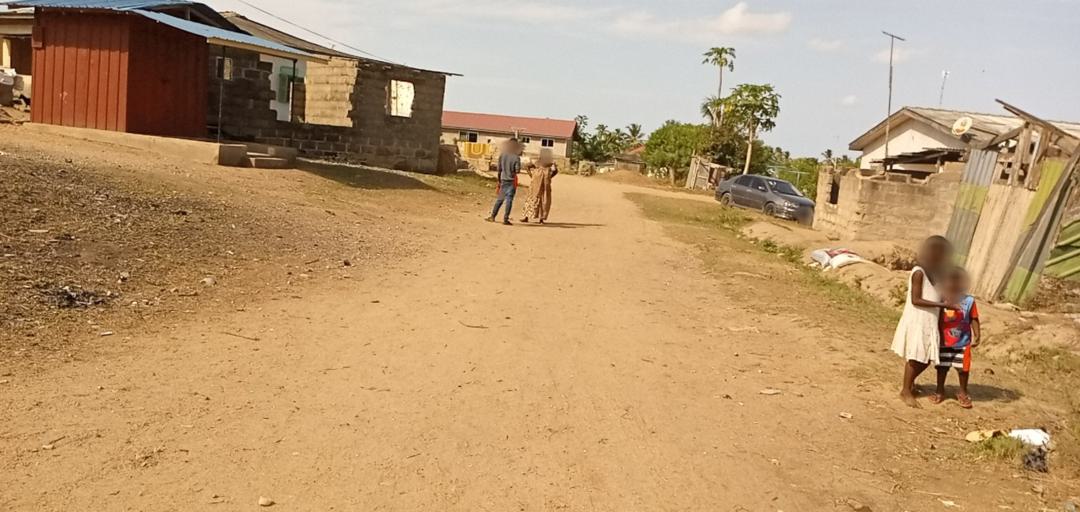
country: GH
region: Central
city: Winneba
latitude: 5.3533
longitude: -0.6213
